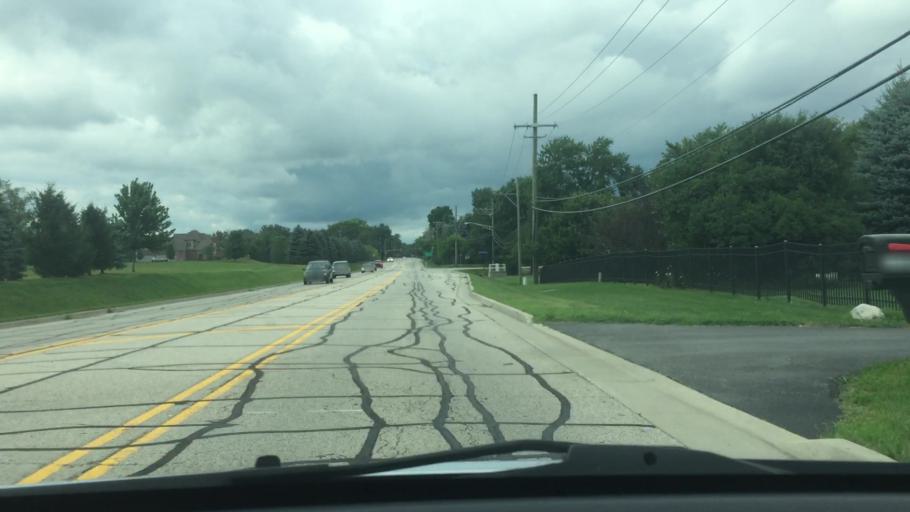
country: US
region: Illinois
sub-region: McHenry County
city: Crystal Lake
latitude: 42.2794
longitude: -88.3209
